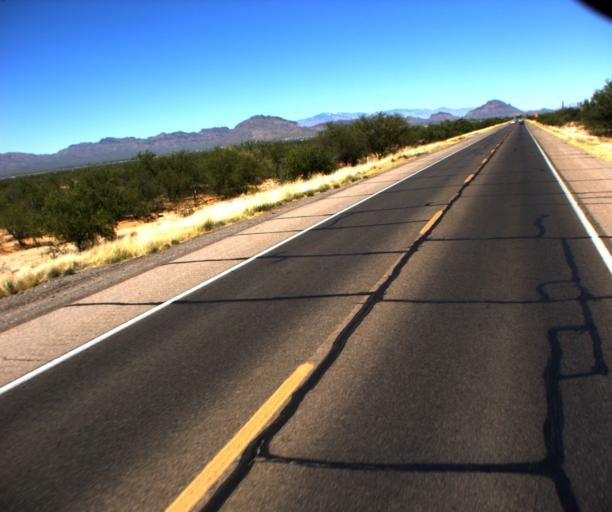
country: US
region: Arizona
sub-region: Pima County
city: Valencia West
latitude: 32.1263
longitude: -111.1927
